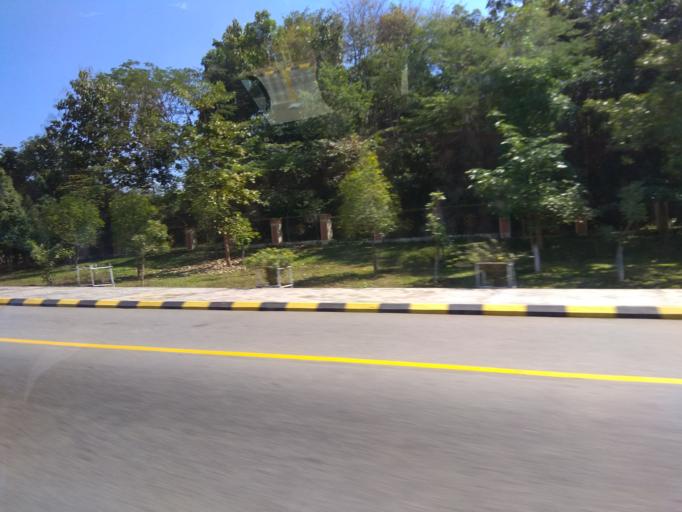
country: MM
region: Mandalay
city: Nay Pyi Taw
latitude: 19.7529
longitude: 96.1243
